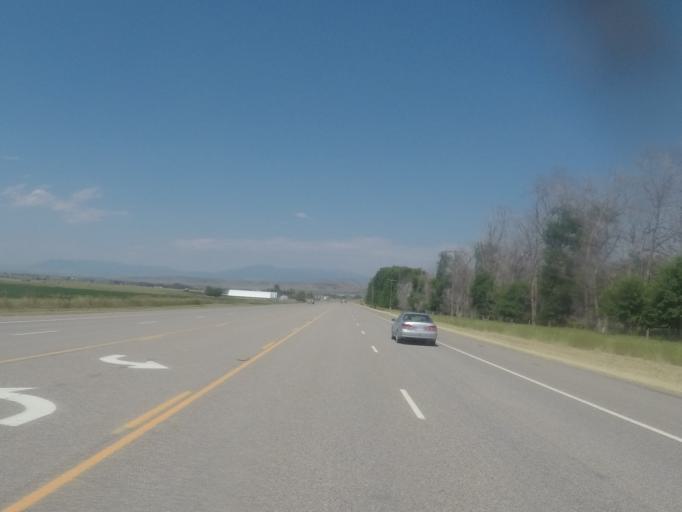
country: US
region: Montana
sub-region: Broadwater County
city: Townsend
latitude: 46.1540
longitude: -111.4642
